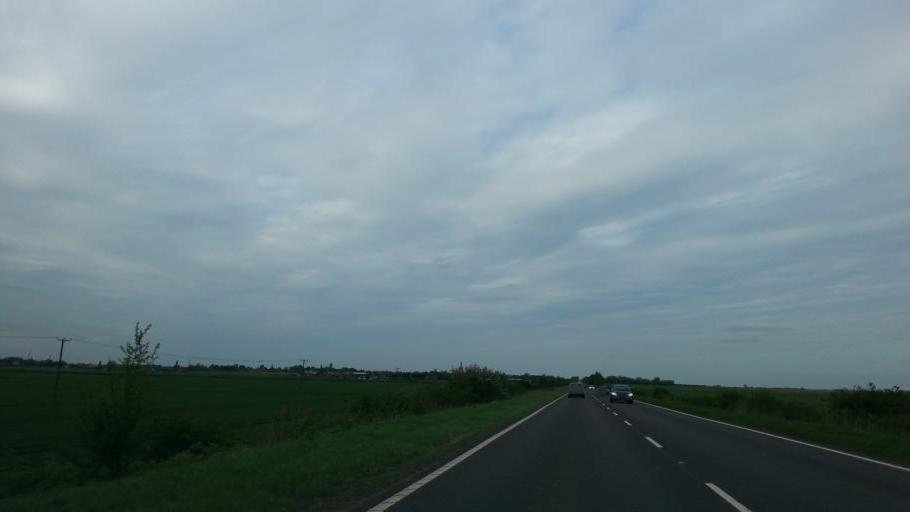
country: GB
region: England
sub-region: Cambridgeshire
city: Chatteris
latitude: 52.4757
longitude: 0.0535
